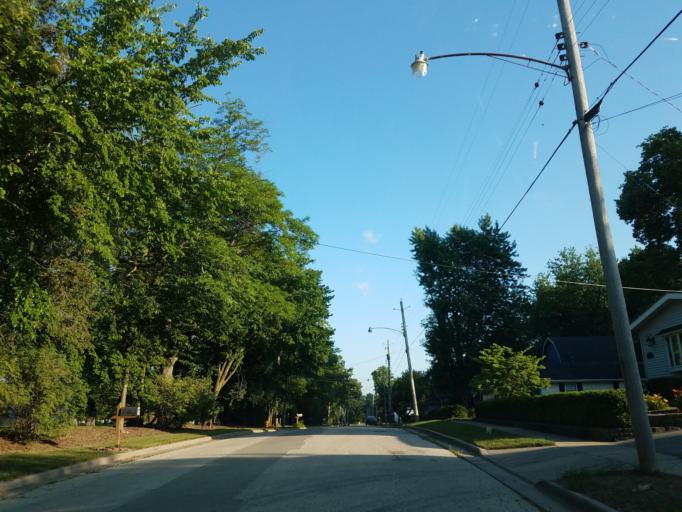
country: US
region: Illinois
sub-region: McLean County
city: Bloomington
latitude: 40.4694
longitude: -89.0098
